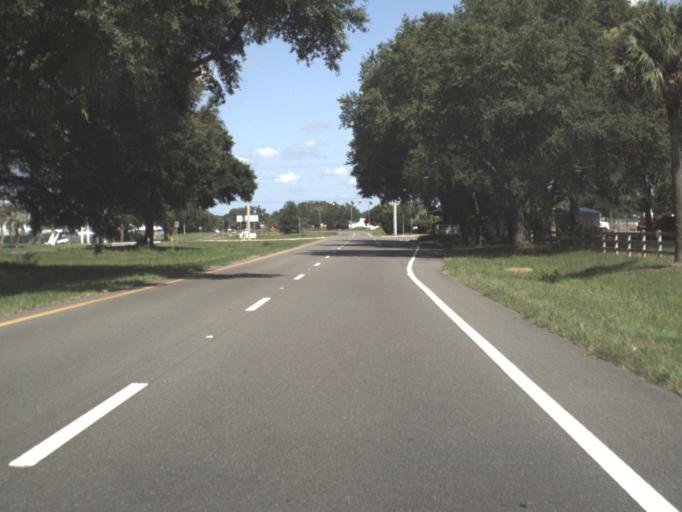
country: US
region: Florida
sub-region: Clay County
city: Green Cove Springs
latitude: 29.9825
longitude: -81.6585
